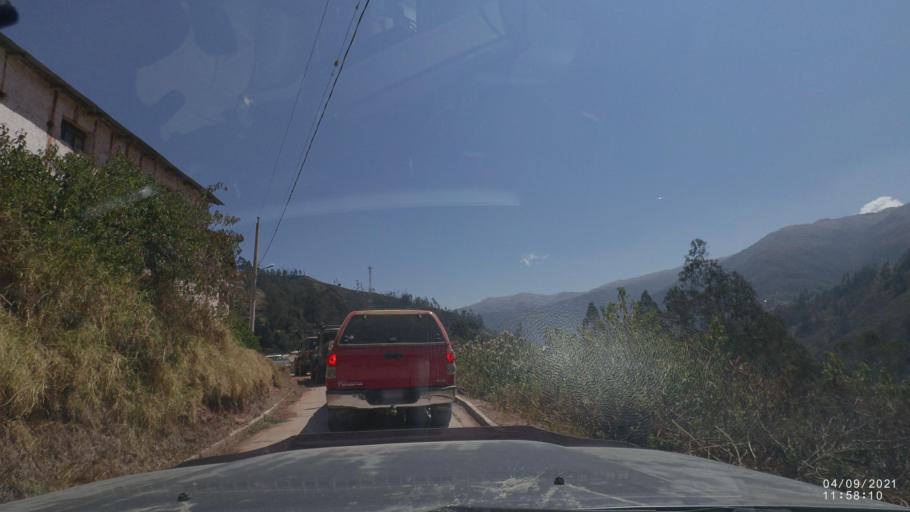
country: BO
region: Cochabamba
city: Colchani
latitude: -17.2374
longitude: -66.5302
